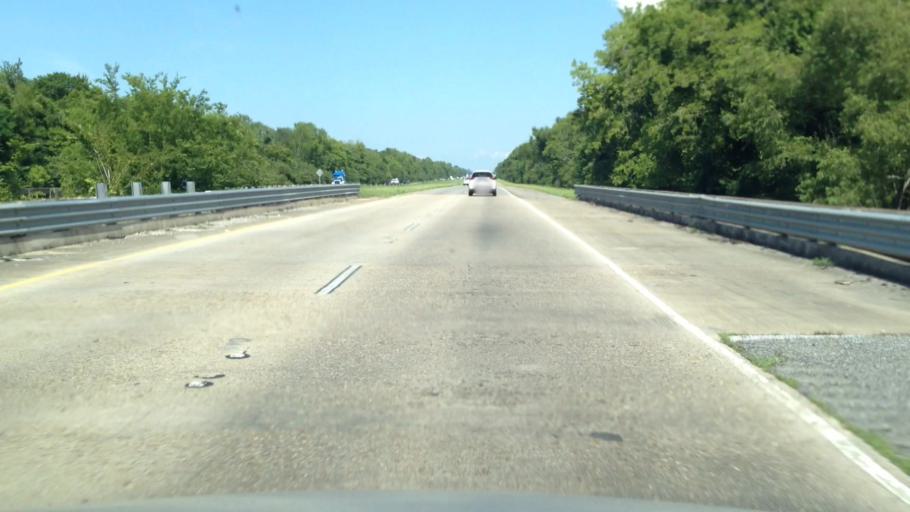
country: US
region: Louisiana
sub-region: Saint John the Baptist Parish
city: Reserve
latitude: 30.1142
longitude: -90.5810
